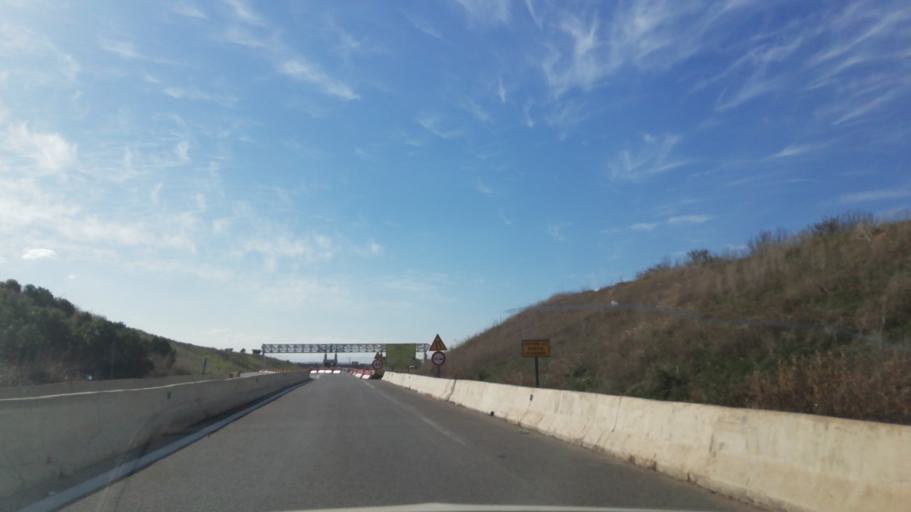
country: DZ
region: Tlemcen
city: Bensekrane
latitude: 34.9850
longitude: -1.2165
